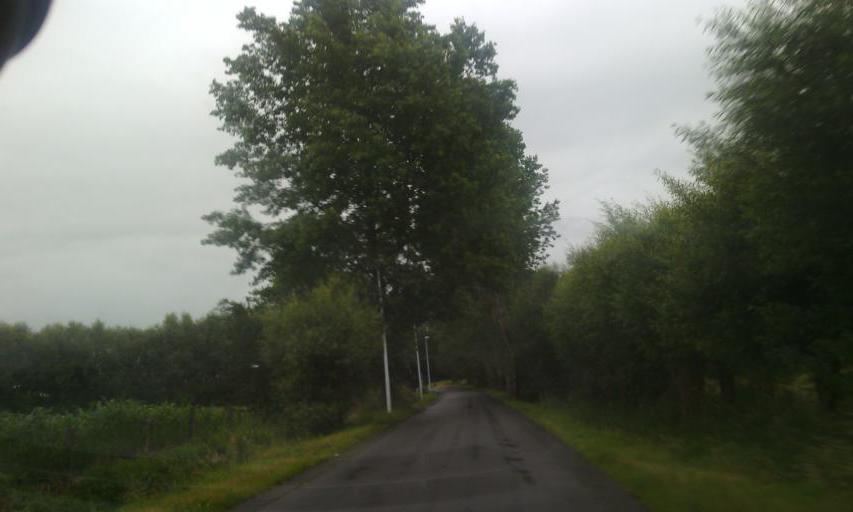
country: BE
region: Flanders
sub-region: Provincie Oost-Vlaanderen
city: Zele
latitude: 51.0765
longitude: 4.0249
